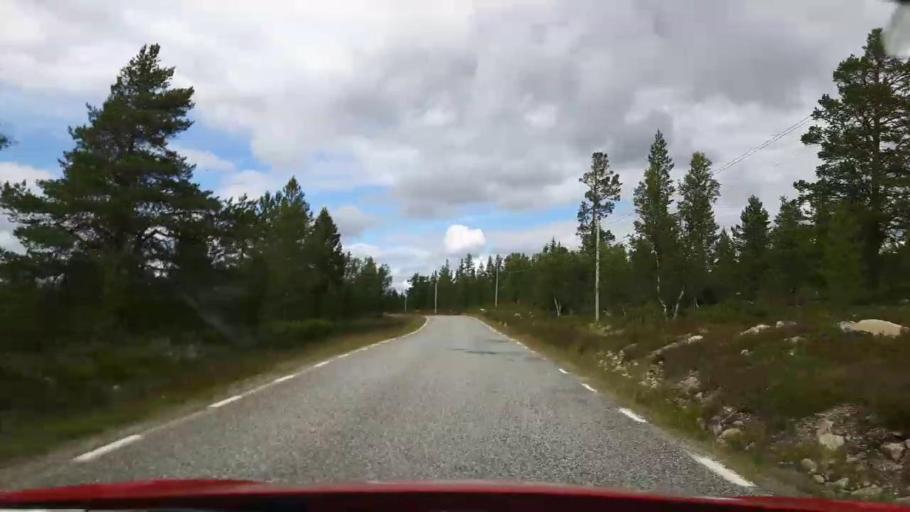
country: NO
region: Hedmark
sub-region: Engerdal
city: Engerdal
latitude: 62.3314
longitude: 12.8068
